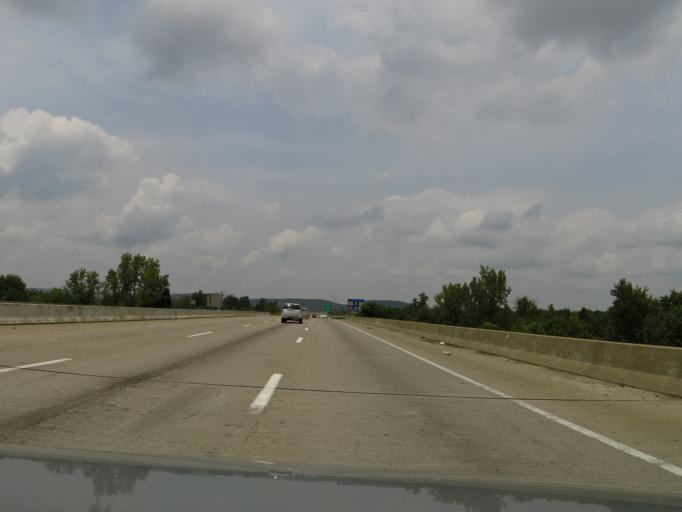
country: US
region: Kentucky
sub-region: Bullitt County
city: Shepherdsville
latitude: 37.9852
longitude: -85.7006
